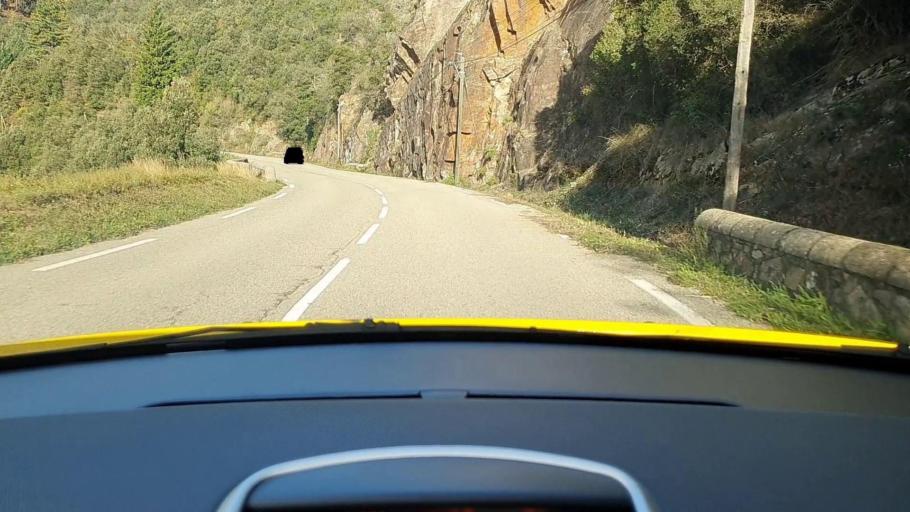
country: FR
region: Languedoc-Roussillon
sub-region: Departement du Gard
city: Lasalle
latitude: 44.1037
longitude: 3.8025
